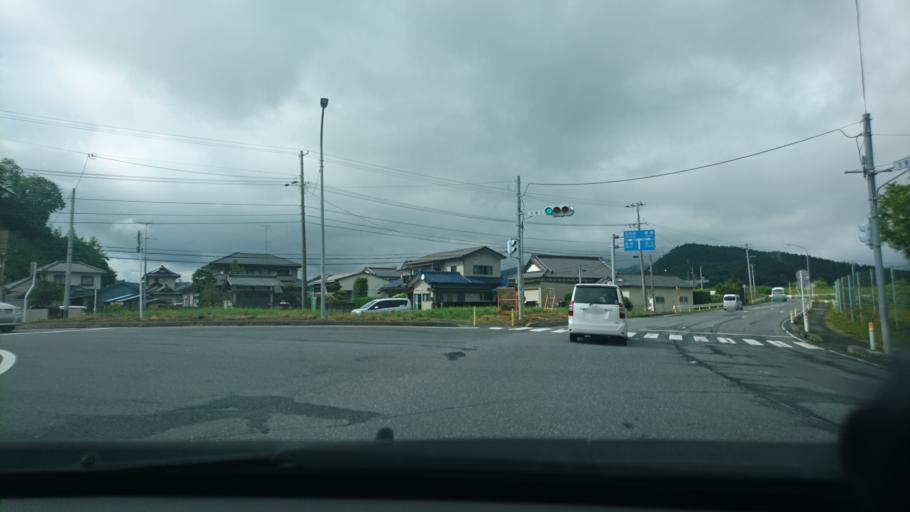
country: JP
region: Miyagi
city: Ishinomaki
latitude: 38.5084
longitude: 141.3093
